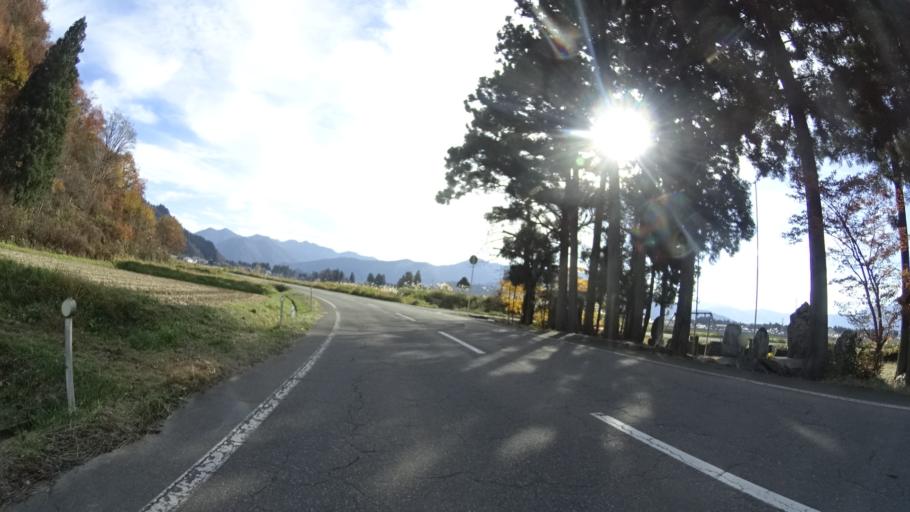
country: JP
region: Niigata
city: Shiozawa
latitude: 37.0237
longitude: 138.8807
